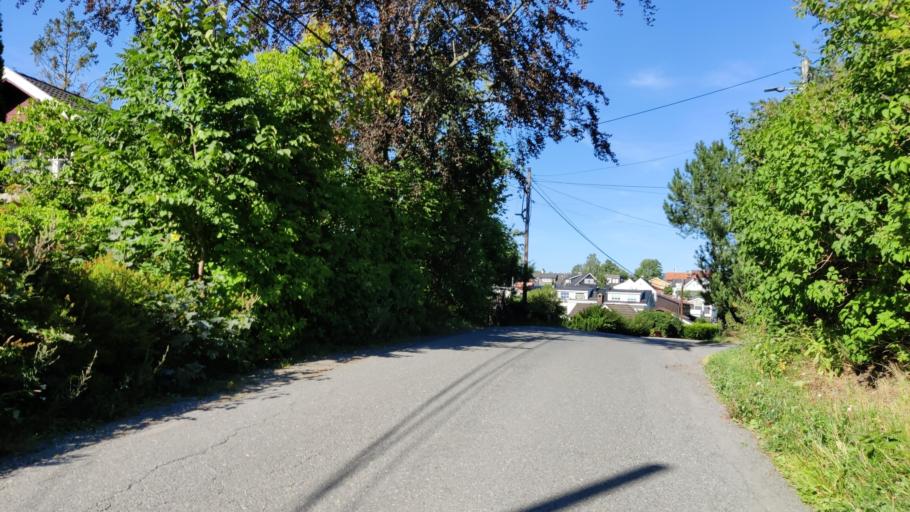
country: NO
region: Akershus
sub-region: Baerum
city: Lysaker
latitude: 59.9235
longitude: 10.5955
